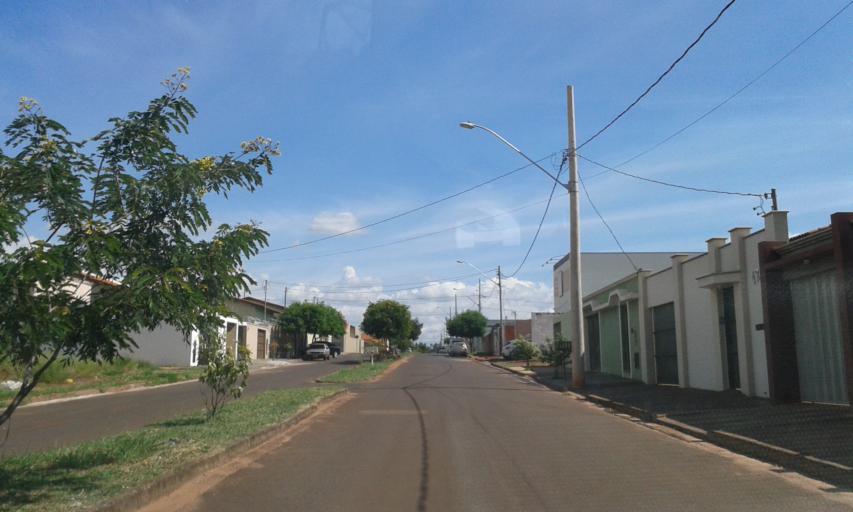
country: BR
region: Minas Gerais
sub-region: Santa Vitoria
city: Santa Vitoria
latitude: -18.8499
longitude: -50.1222
